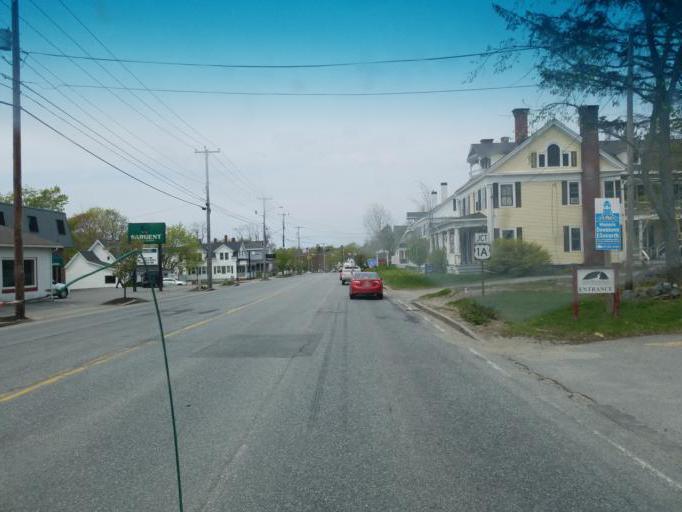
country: US
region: Maine
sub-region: Hancock County
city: Ellsworth
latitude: 44.5417
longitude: -68.4185
